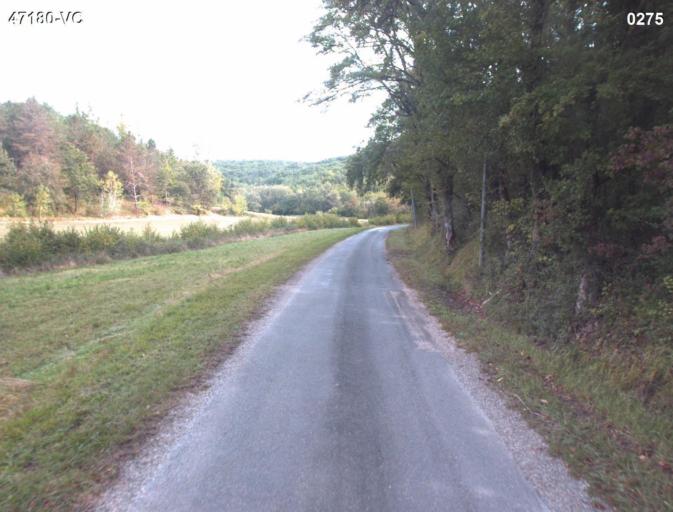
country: FR
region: Aquitaine
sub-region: Departement du Lot-et-Garonne
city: Sainte-Colombe-en-Bruilhois
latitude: 44.1868
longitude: 0.4413
